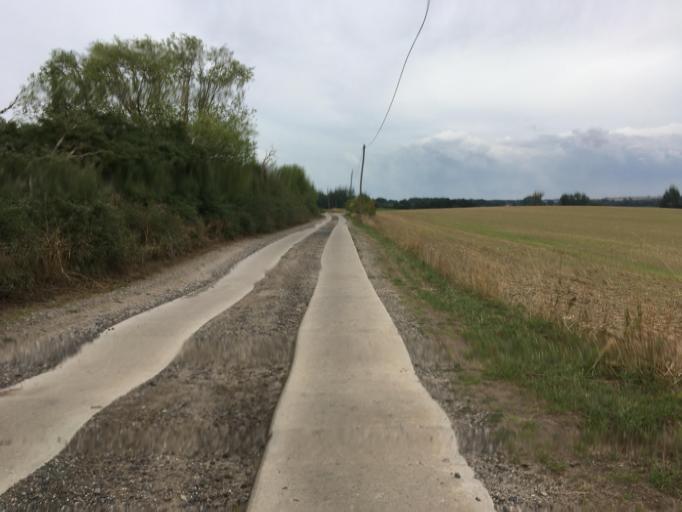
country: DE
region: Brandenburg
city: Gerswalde
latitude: 53.1990
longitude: 13.8302
